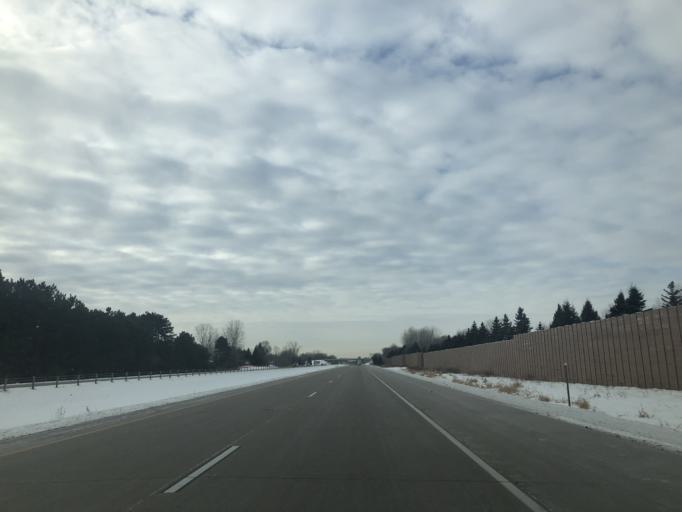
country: US
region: Minnesota
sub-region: Anoka County
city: Circle Pines
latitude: 45.1705
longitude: -93.1342
